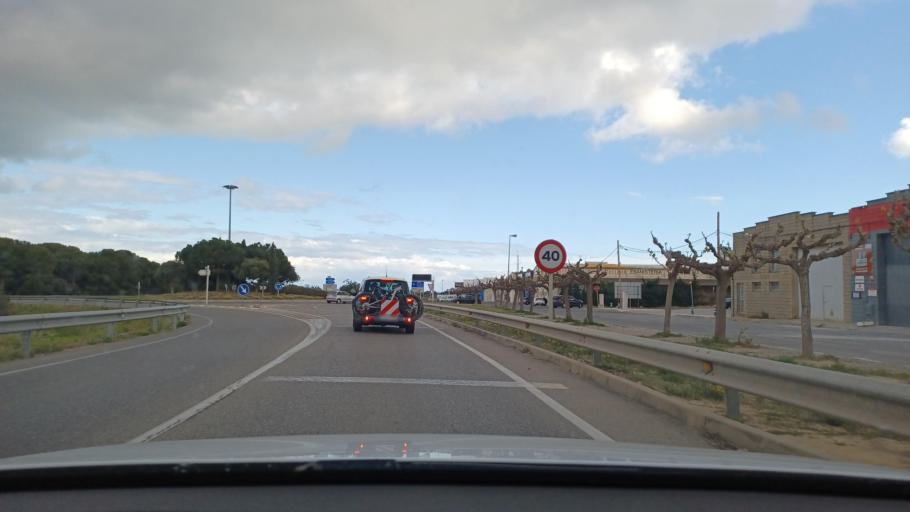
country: ES
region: Catalonia
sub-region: Provincia de Tarragona
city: Cambrils
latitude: 41.0792
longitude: 1.0395
